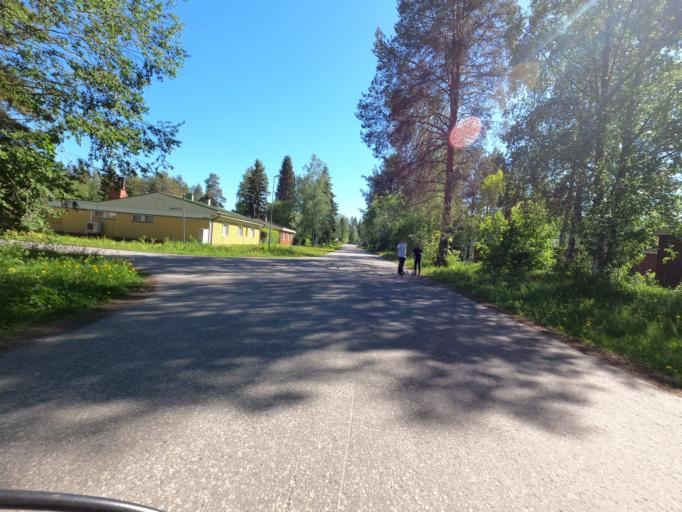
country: FI
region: North Karelia
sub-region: Joensuu
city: Joensuu
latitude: 62.5966
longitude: 29.8113
